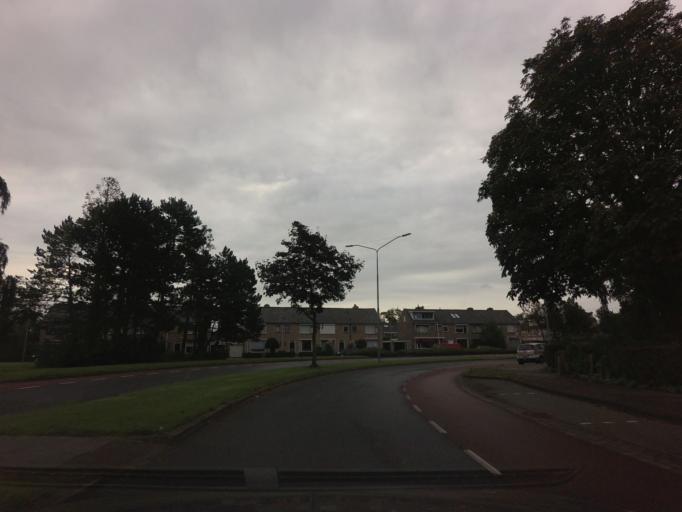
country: NL
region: North Holland
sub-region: Gemeente Alkmaar
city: Alkmaar
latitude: 52.6357
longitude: 4.7779
